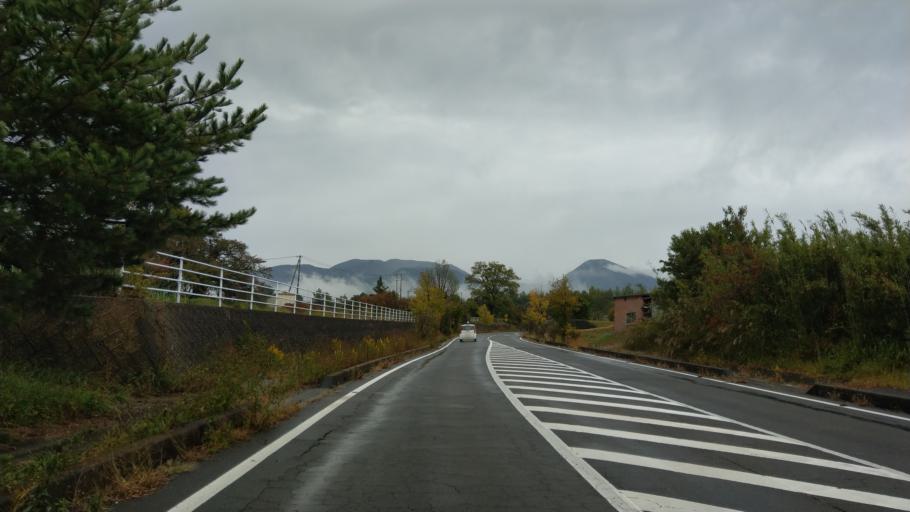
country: JP
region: Nagano
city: Komoro
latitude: 36.3417
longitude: 138.4046
